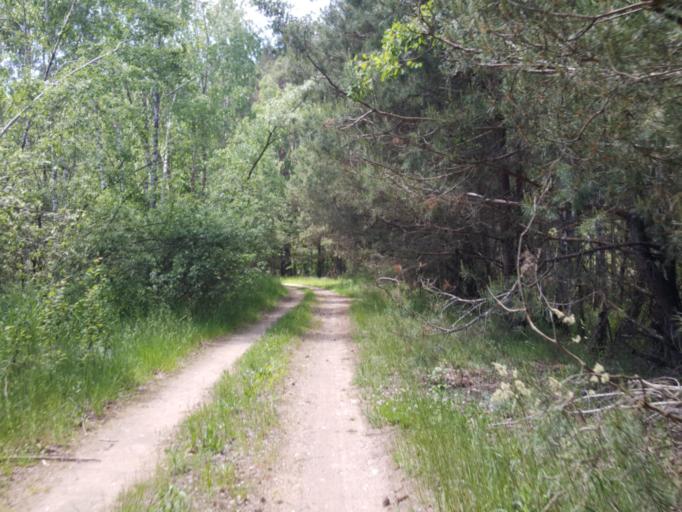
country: BY
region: Brest
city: Kamyanyuki
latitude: 52.5443
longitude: 23.6924
